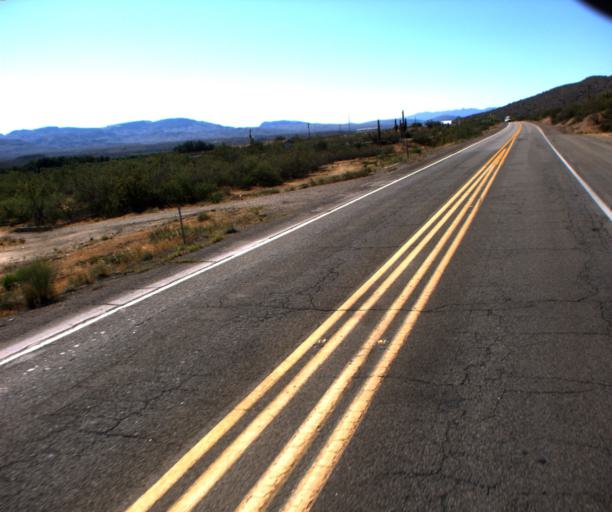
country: US
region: Arizona
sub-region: Yavapai County
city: Bagdad
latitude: 34.6968
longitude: -113.6081
